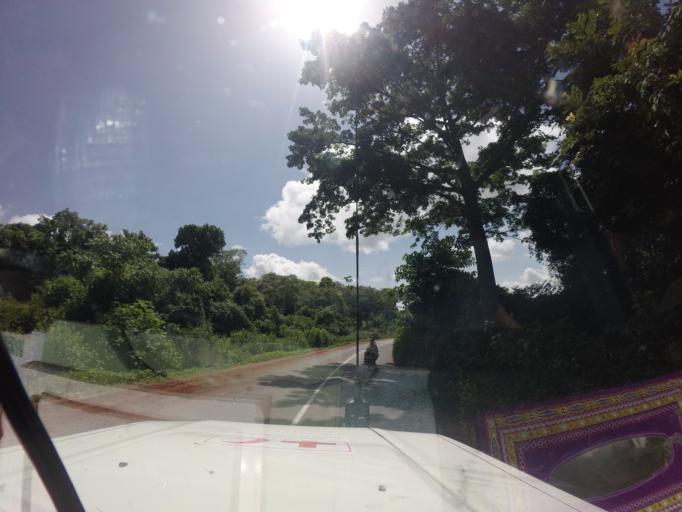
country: GN
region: Mamou
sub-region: Mamou Prefecture
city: Mamou
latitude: 10.1805
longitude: -11.7800
